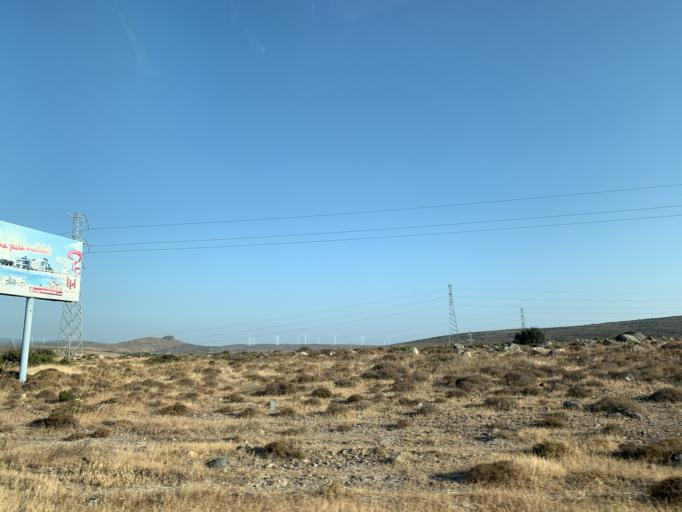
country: TR
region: Izmir
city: Alacati
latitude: 38.2771
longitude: 26.4211
